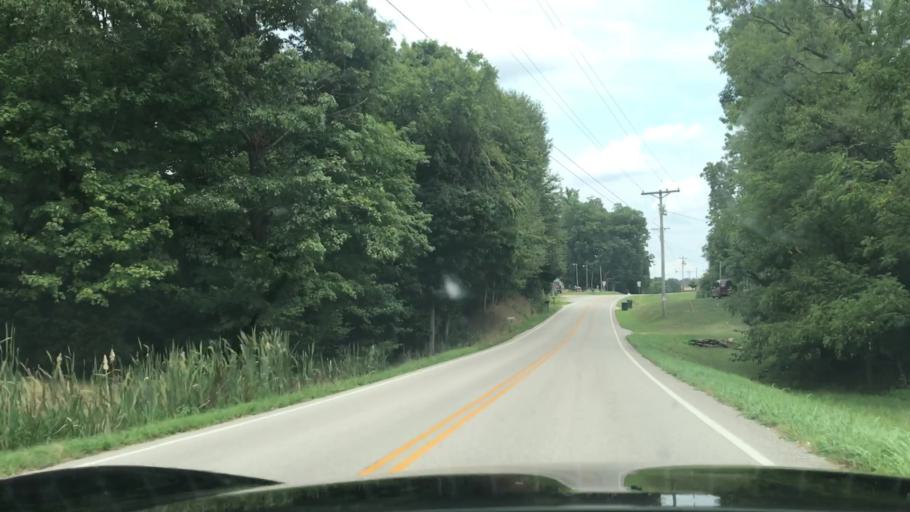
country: US
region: Kentucky
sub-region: Butler County
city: Morgantown
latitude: 37.1879
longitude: -86.7592
